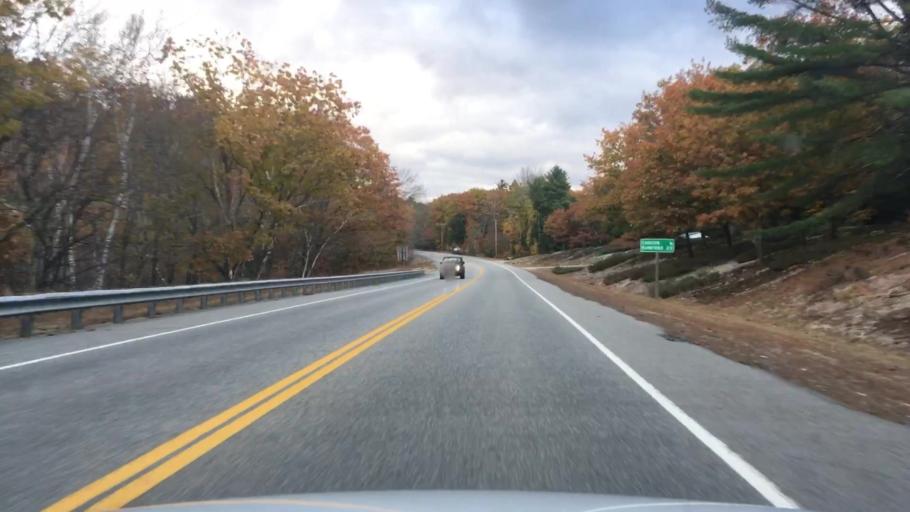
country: US
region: Maine
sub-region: Androscoggin County
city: Livermore
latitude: 44.3900
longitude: -70.2561
